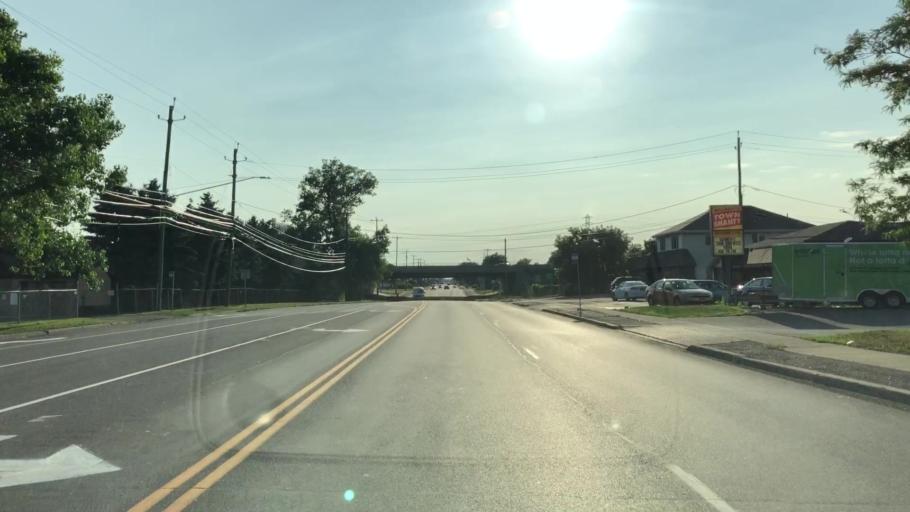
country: US
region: New York
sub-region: Erie County
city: Sloan
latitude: 42.8715
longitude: -78.7877
